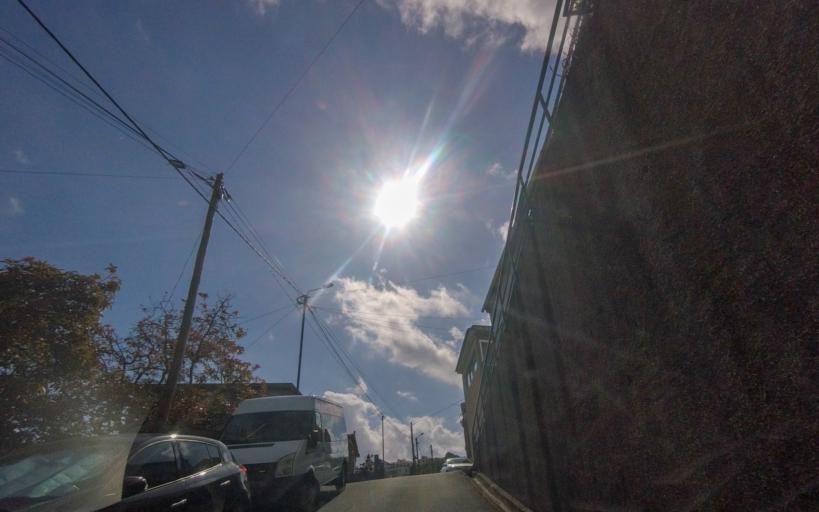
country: PT
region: Madeira
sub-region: Funchal
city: Nossa Senhora do Monte
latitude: 32.6741
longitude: -16.9447
